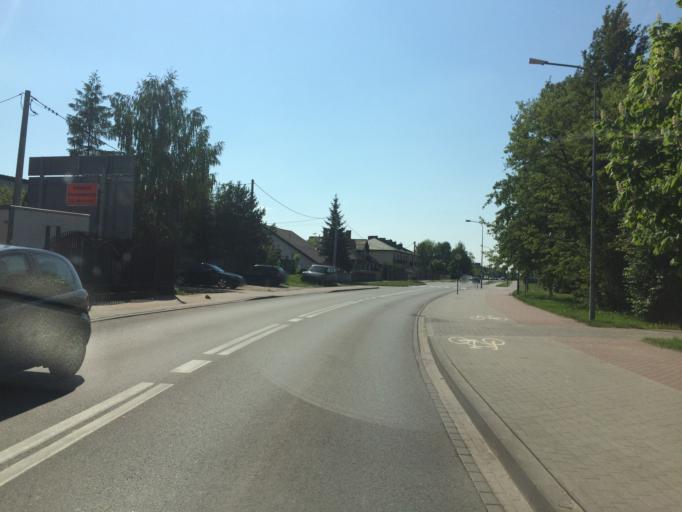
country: PL
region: Masovian Voivodeship
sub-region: Powiat wolominski
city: Zabki
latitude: 52.3012
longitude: 21.0944
